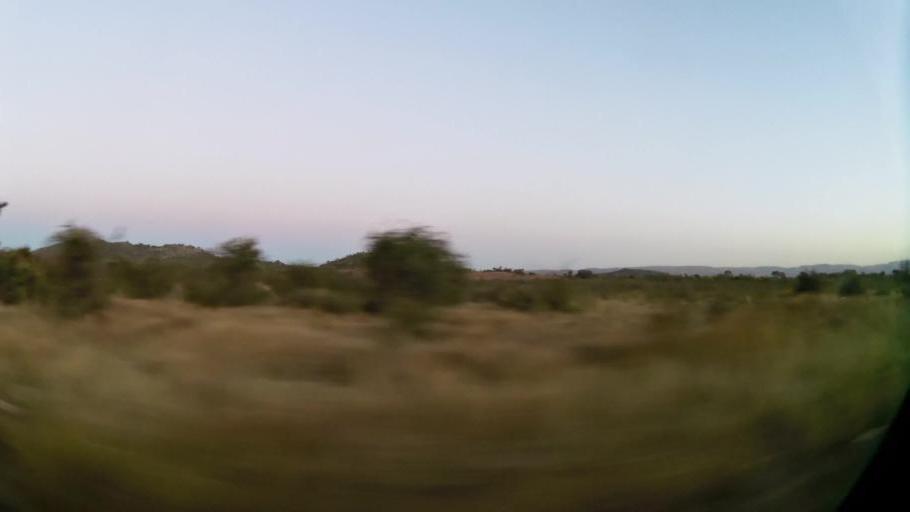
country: ZA
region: North-West
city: Ga-Rankuwa
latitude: -25.6306
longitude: 27.9590
